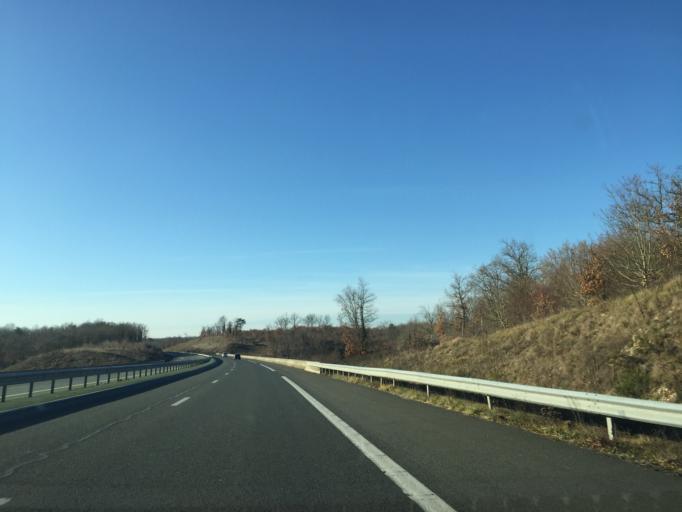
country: FR
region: Aquitaine
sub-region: Departement de la Dordogne
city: Thenon
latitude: 45.1755
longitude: 1.0167
